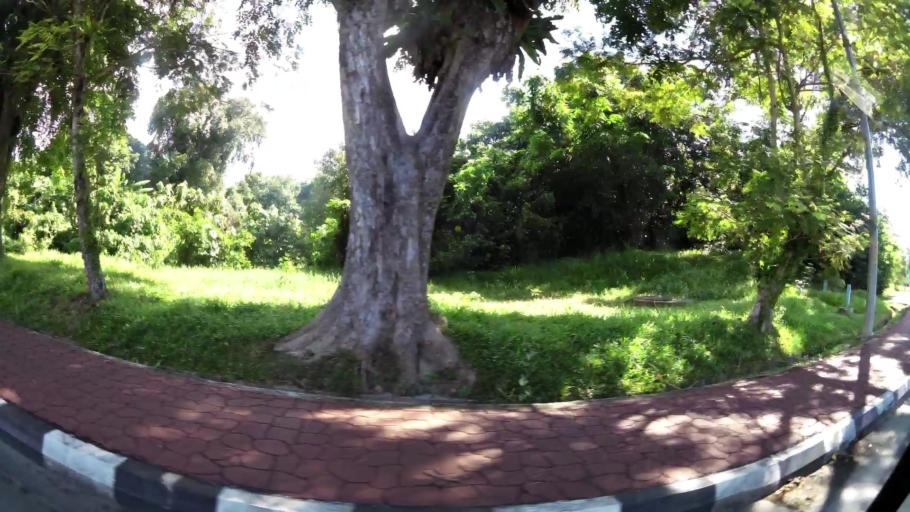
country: BN
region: Brunei and Muara
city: Bandar Seri Begawan
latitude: 4.9423
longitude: 114.9397
